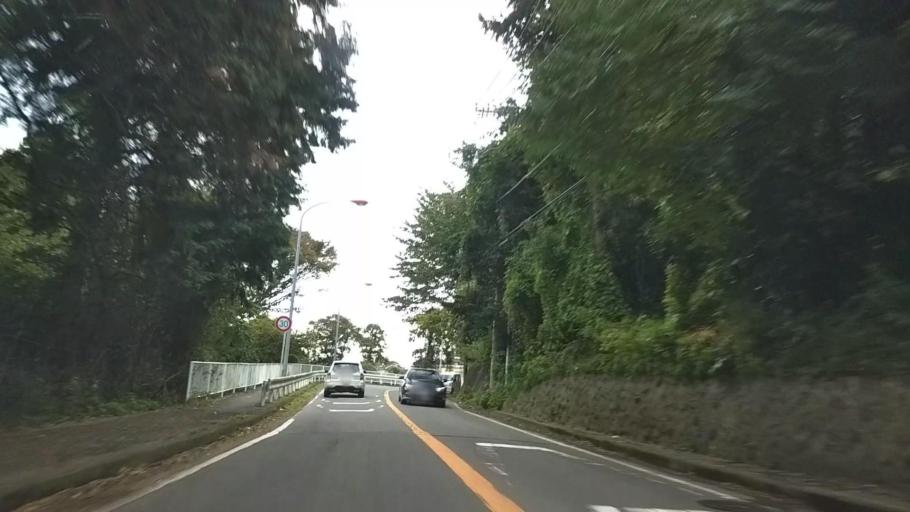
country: JP
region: Kanagawa
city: Yugawara
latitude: 35.1651
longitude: 139.1349
